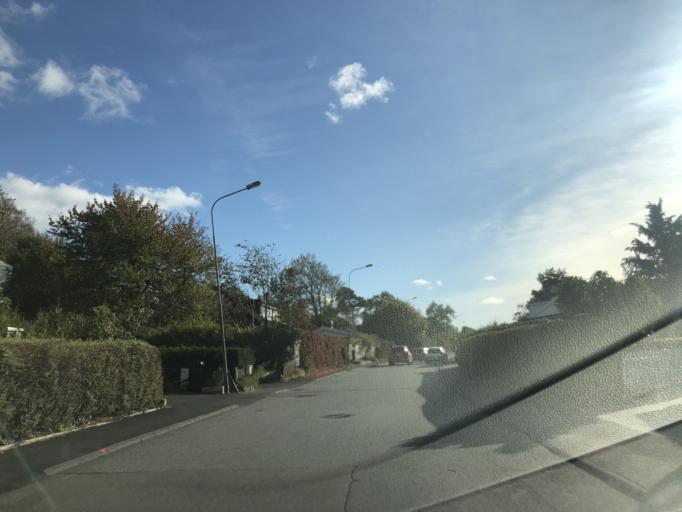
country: SE
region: Vaestra Goetaland
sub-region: Goteborg
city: Billdal
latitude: 57.6281
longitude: 11.9363
